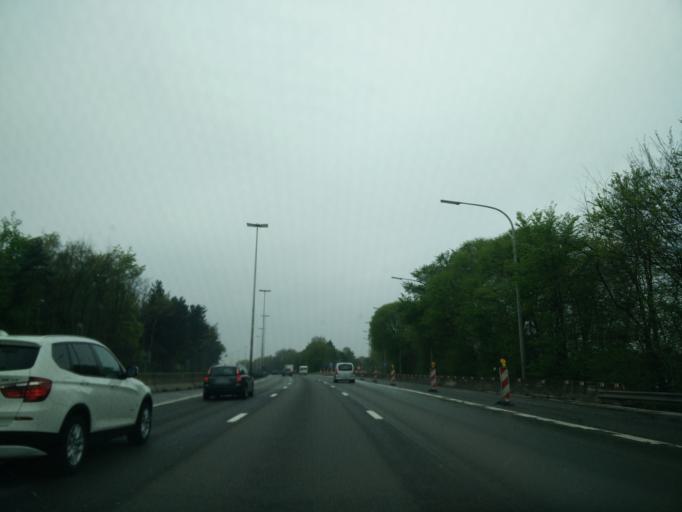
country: BE
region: Wallonia
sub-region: Province de Liege
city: Herstal
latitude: 50.6891
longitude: 5.6198
